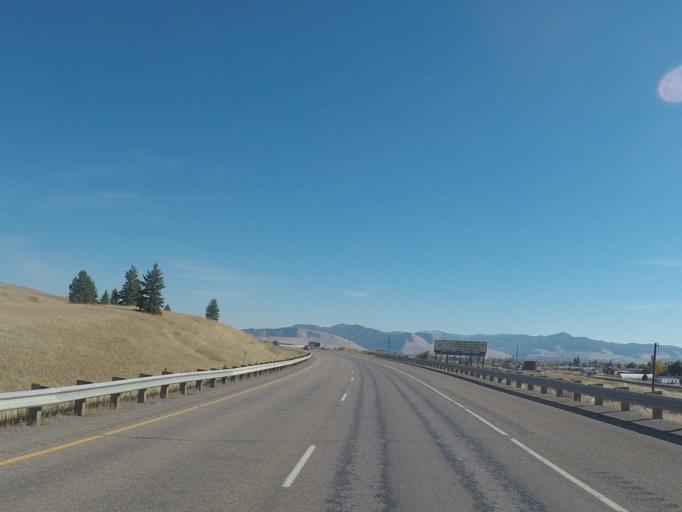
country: US
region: Montana
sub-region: Missoula County
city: Orchard Homes
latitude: 46.9401
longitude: -114.1118
